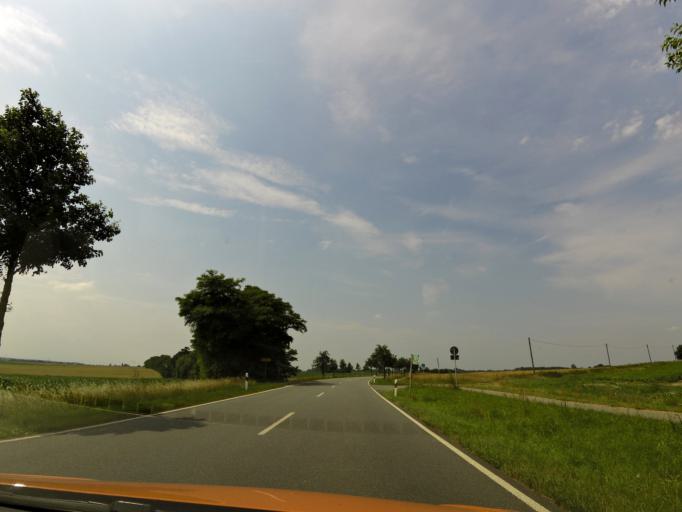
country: DE
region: Brandenburg
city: Kyritz
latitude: 52.9653
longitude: 12.3837
